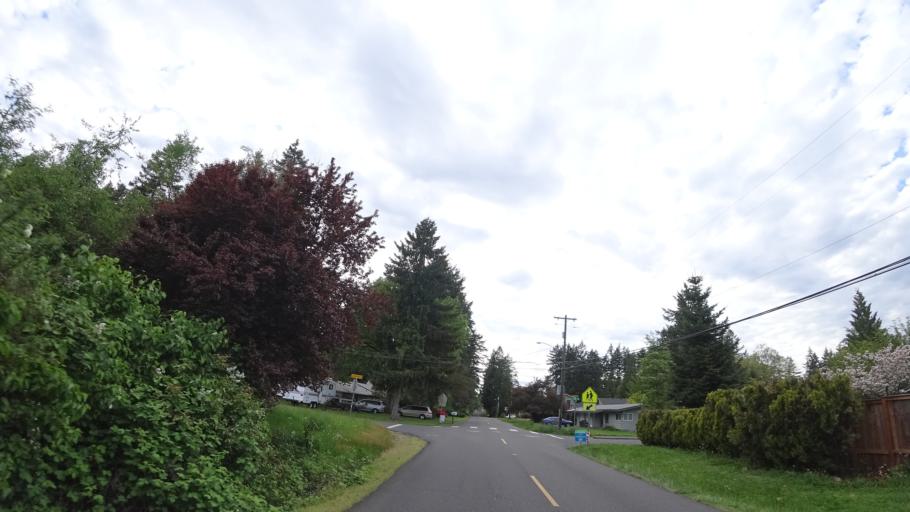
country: US
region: Oregon
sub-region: Washington County
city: Hillsboro
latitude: 45.5122
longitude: -122.9411
